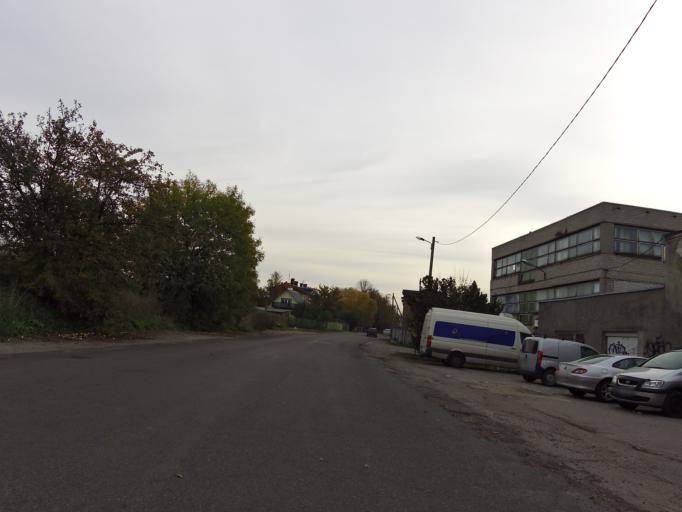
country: EE
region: Harju
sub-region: Tallinna linn
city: Tallinn
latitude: 59.4424
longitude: 24.7183
